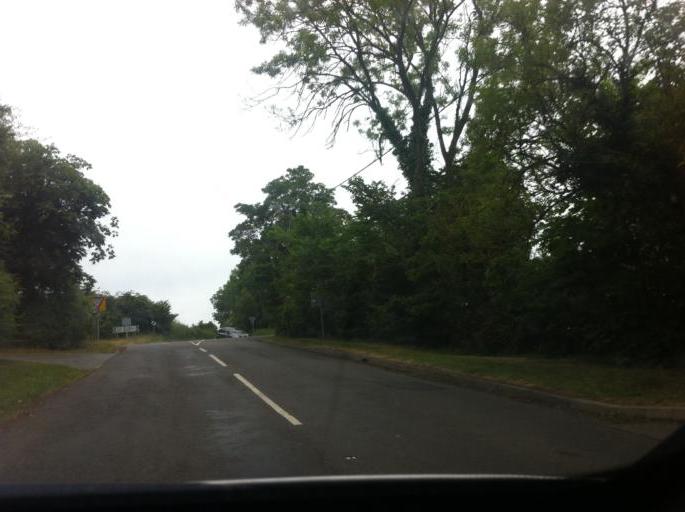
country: GB
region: England
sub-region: Northamptonshire
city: Earls Barton
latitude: 52.2691
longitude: -0.7216
